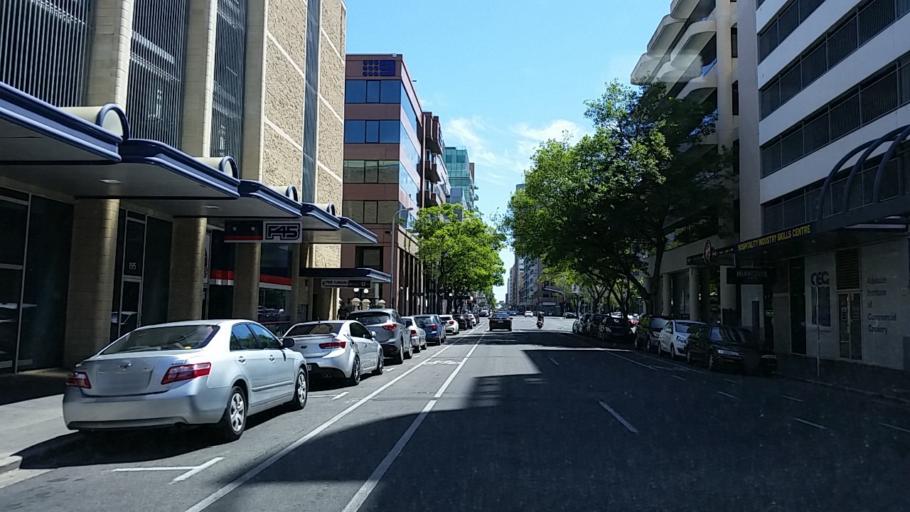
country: AU
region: South Australia
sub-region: Adelaide
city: Adelaide
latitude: -34.9254
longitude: 138.6075
